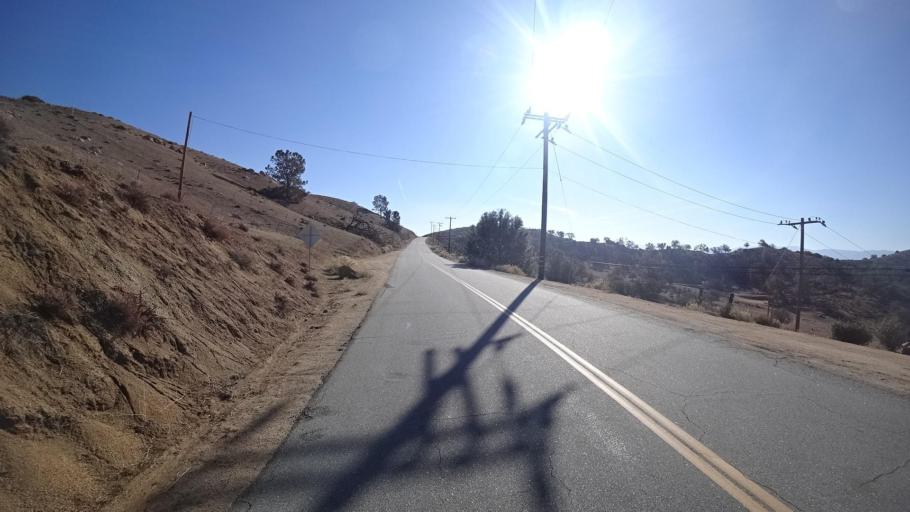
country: US
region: California
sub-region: Kern County
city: Bodfish
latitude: 35.3716
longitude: -118.3996
